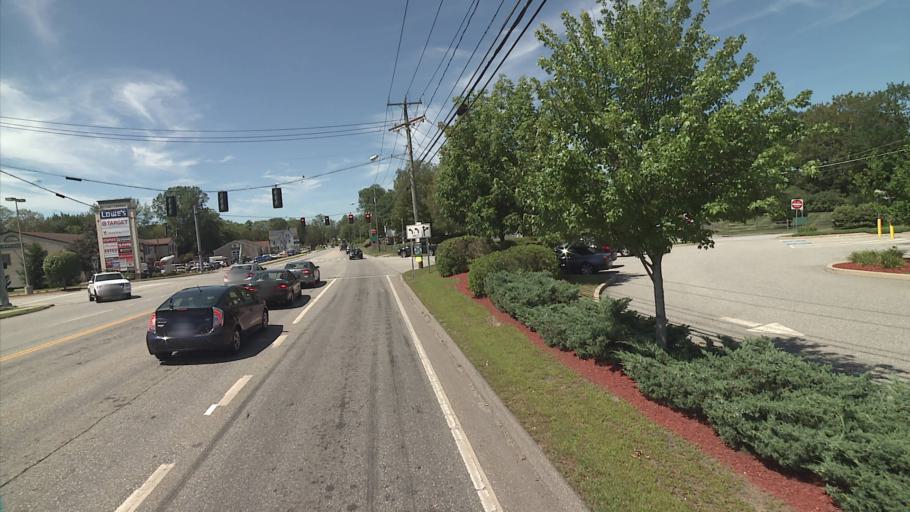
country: US
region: Connecticut
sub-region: Windham County
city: Killingly Center
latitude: 41.8440
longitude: -71.8817
